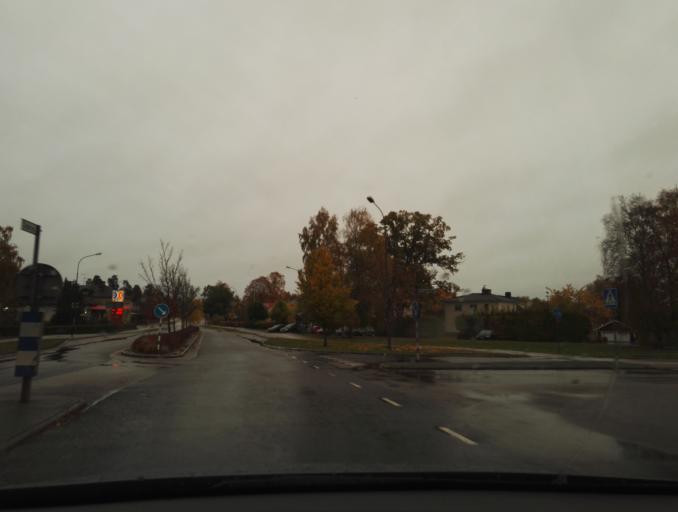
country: SE
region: Kronoberg
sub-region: Vaxjo Kommun
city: Vaexjoe
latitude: 56.8859
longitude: 14.7511
